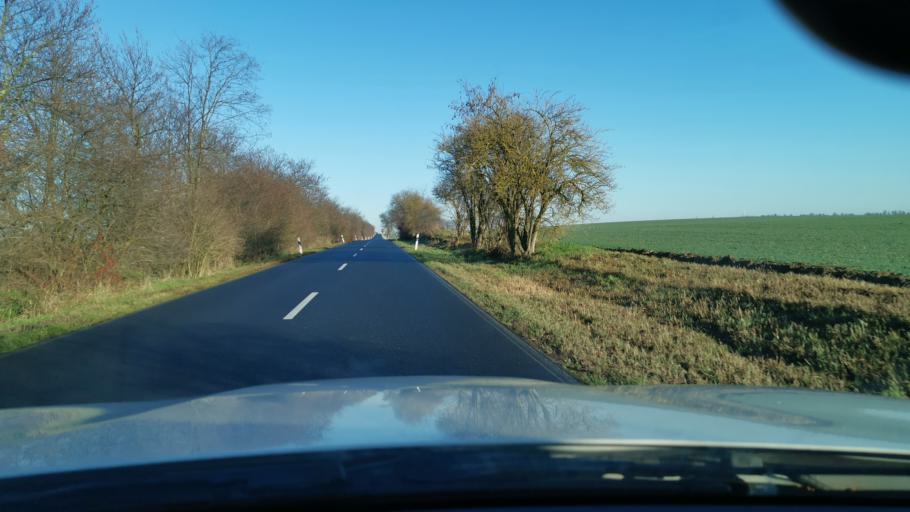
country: DE
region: Saxony-Anhalt
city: Seyda
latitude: 51.9641
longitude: 12.9008
